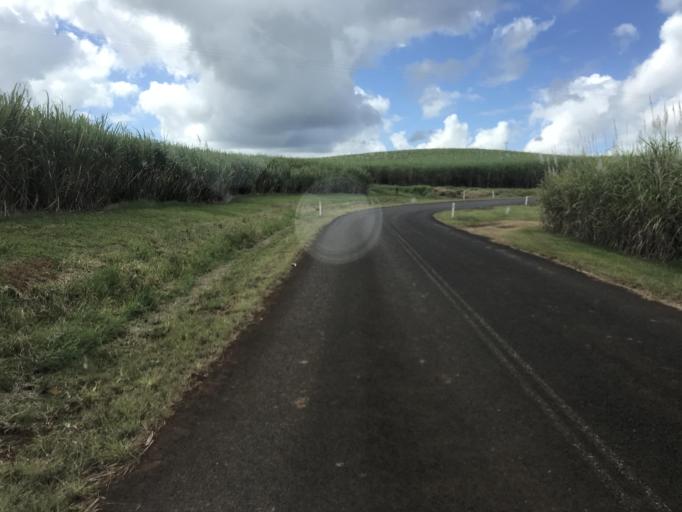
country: AU
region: Queensland
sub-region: Cassowary Coast
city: Innisfail
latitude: -17.5489
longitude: 145.8739
